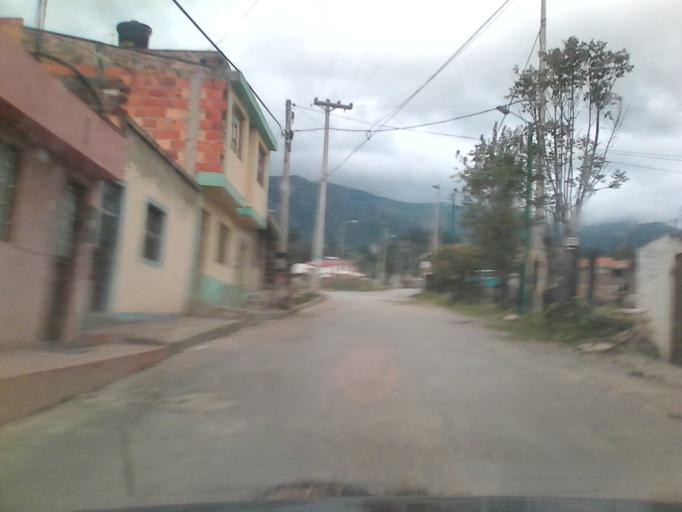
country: CO
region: Boyaca
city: Duitama
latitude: 5.8442
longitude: -73.0360
